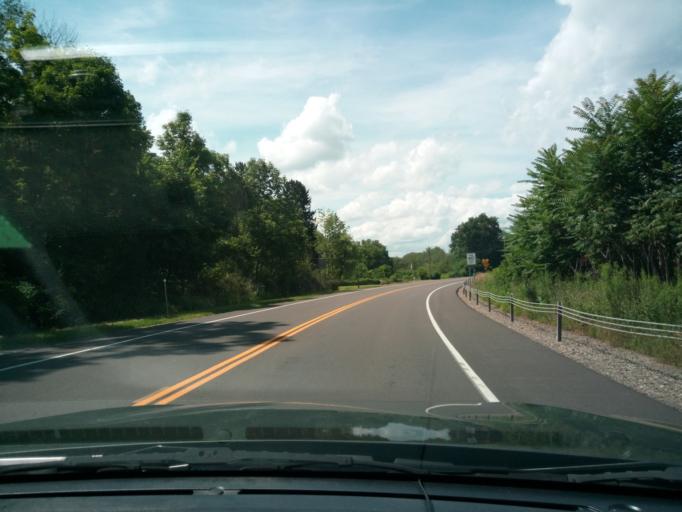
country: US
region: New York
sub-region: Chemung County
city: Southport
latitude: 42.0226
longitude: -76.7403
